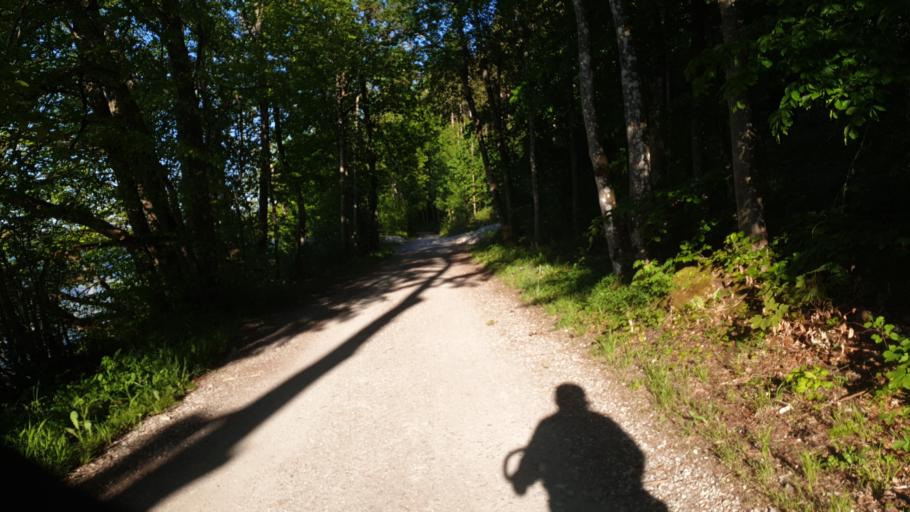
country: DE
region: Bavaria
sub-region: Upper Bavaria
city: Seehausen am Staffelsee
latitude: 47.6780
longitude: 11.1564
